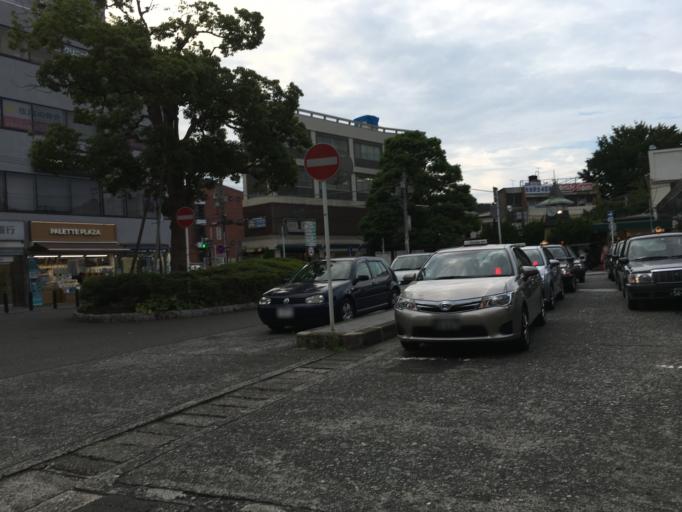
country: JP
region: Kanagawa
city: Kamakura
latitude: 35.3188
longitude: 139.5500
